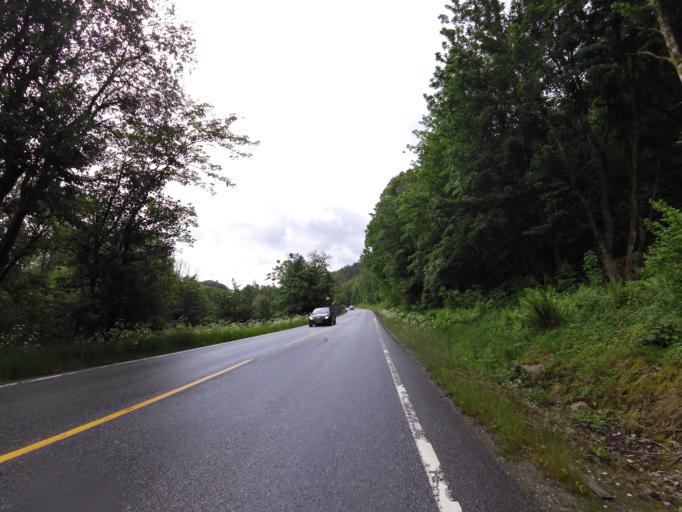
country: NO
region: Vest-Agder
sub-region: Farsund
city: Farsund
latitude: 58.1014
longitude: 6.8619
